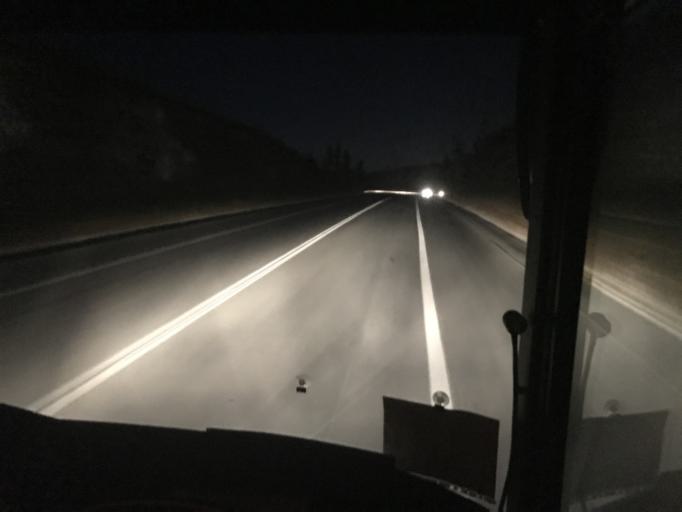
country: GR
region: Crete
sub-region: Nomos Irakleiou
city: Skalanion
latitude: 35.2780
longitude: 25.1815
